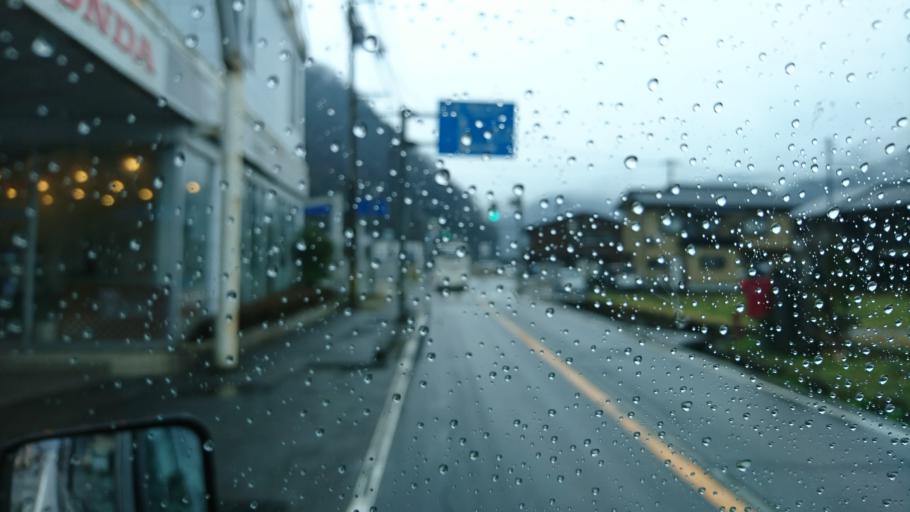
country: JP
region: Tottori
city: Tottori
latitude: 35.5831
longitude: 134.4896
